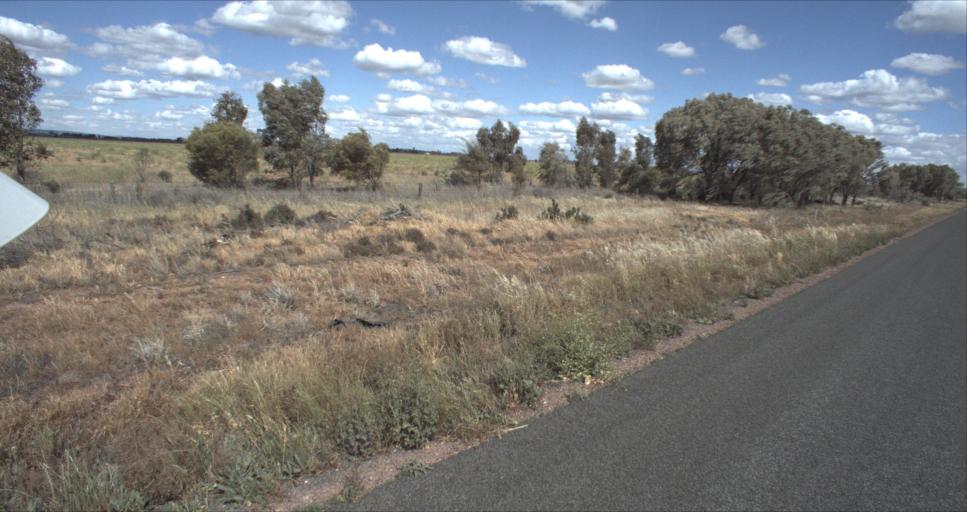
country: AU
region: New South Wales
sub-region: Leeton
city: Leeton
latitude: -34.4356
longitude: 146.2574
